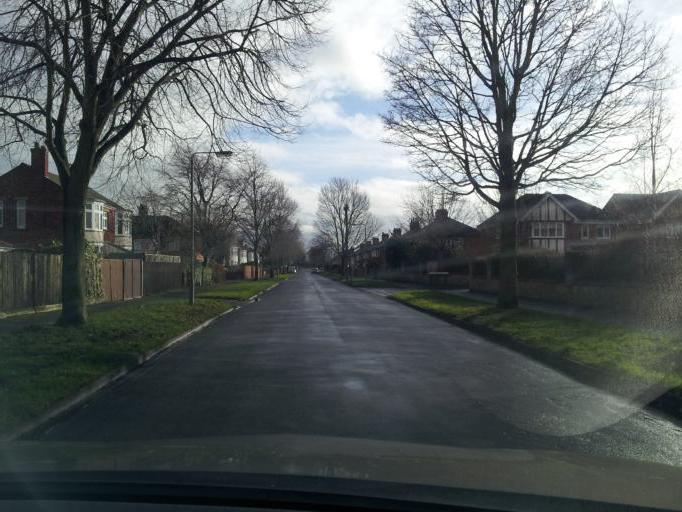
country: GB
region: England
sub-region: Nottinghamshire
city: Newark on Trent
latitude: 53.0685
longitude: -0.8134
